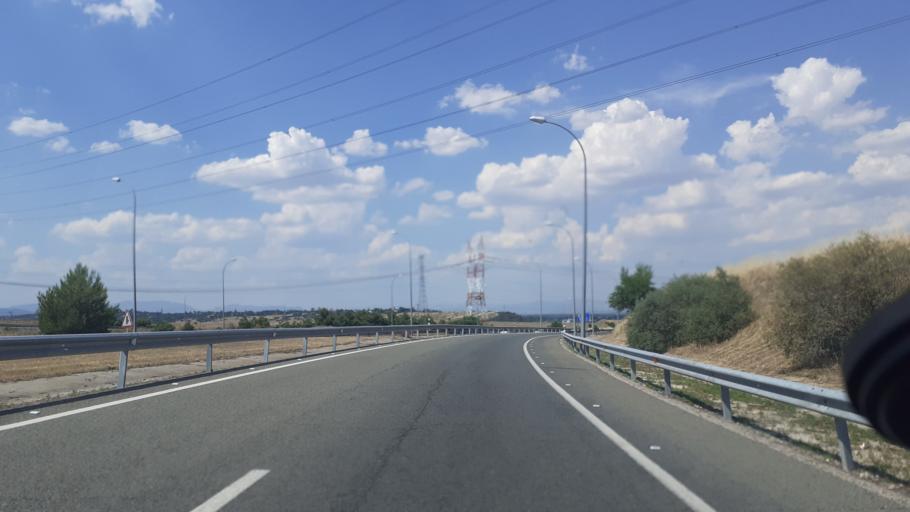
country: ES
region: Madrid
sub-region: Provincia de Madrid
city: San Sebastian de los Reyes
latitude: 40.5636
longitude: -3.5919
